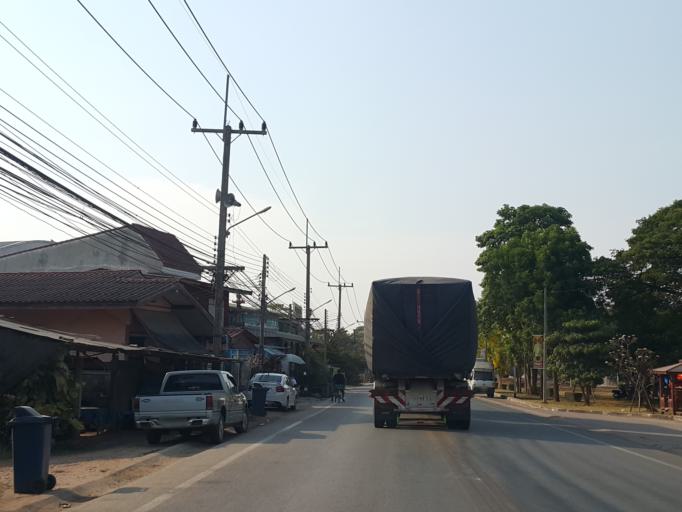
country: TH
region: Phitsanulok
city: Phrom Phiram
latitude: 17.0279
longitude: 100.2020
